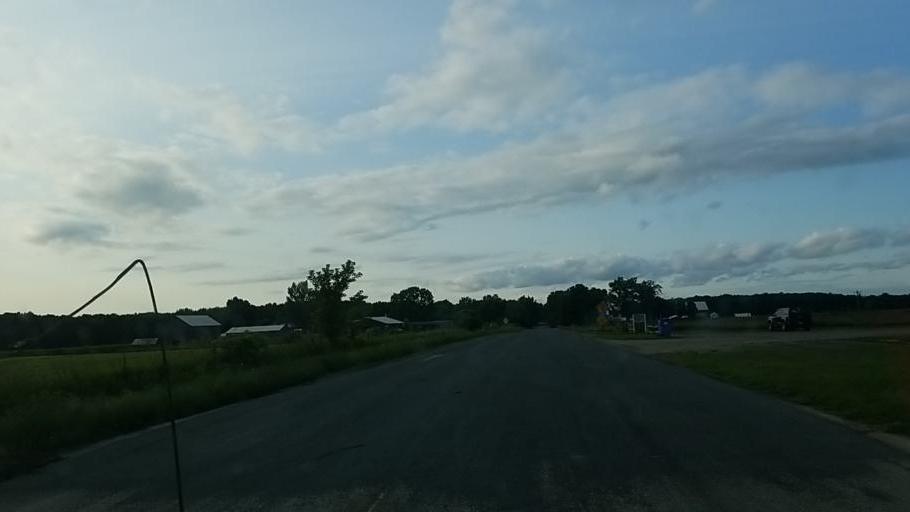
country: US
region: Michigan
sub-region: Montcalm County
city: Lakeview
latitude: 43.3594
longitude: -85.3230
